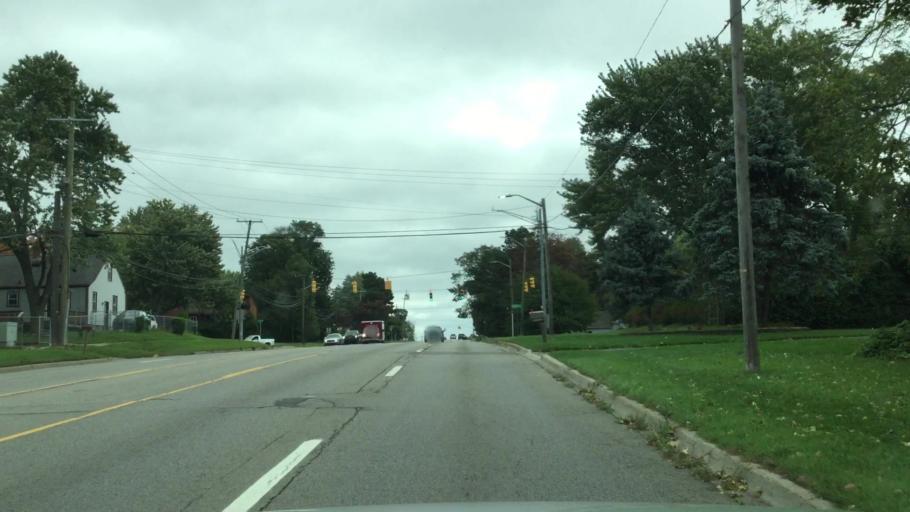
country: US
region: Michigan
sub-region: Oakland County
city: Keego Harbor
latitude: 42.6394
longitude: -83.3469
